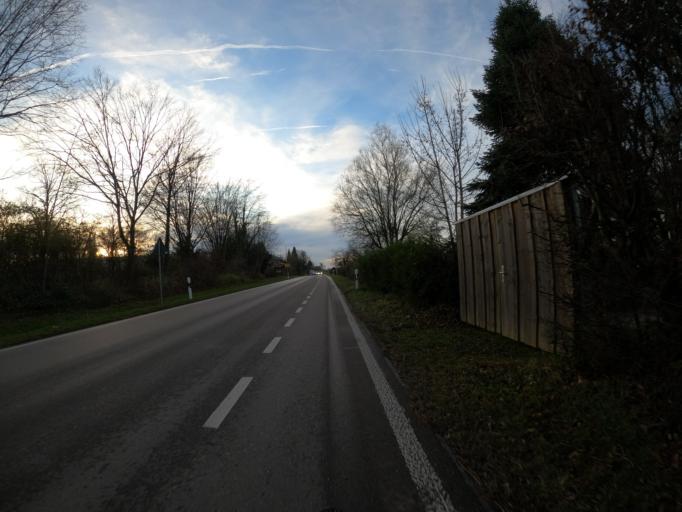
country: DE
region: Baden-Wuerttemberg
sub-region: Regierungsbezirk Stuttgart
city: Hattenhofen
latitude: 48.6661
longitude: 9.5602
